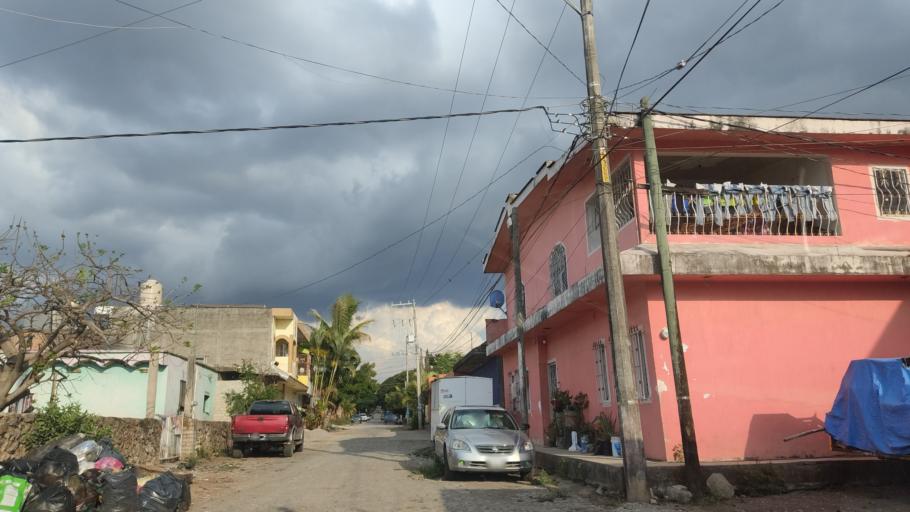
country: MX
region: Nayarit
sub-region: Tepic
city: La Corregidora
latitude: 21.4509
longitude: -104.8152
